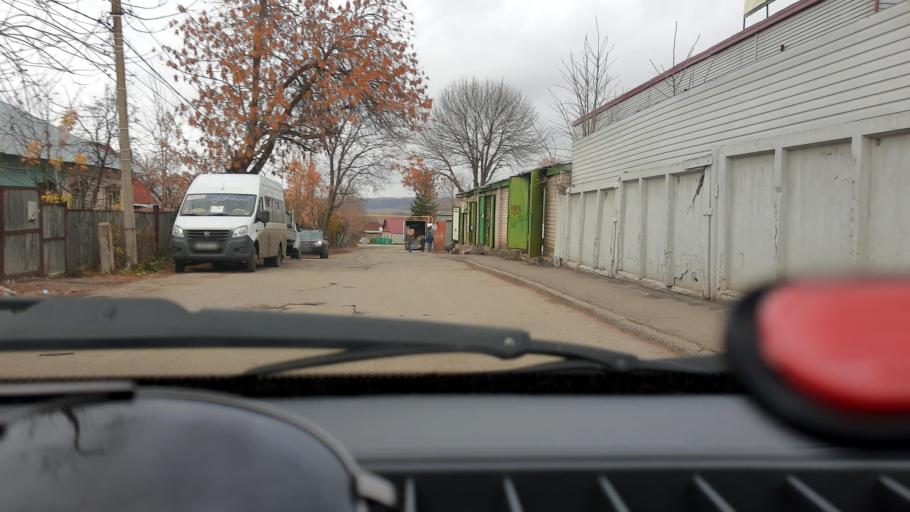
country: RU
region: Bashkortostan
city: Ufa
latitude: 54.8292
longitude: 56.0682
